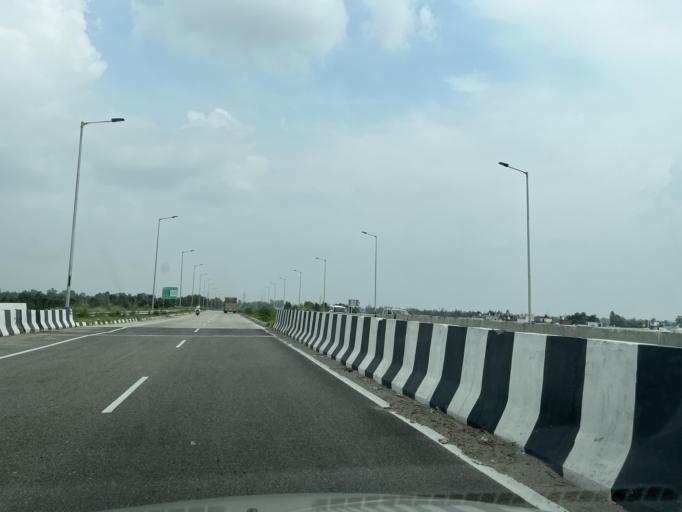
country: IN
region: Uttarakhand
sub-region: Udham Singh Nagar
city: Kashipur
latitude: 29.1731
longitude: 78.9475
